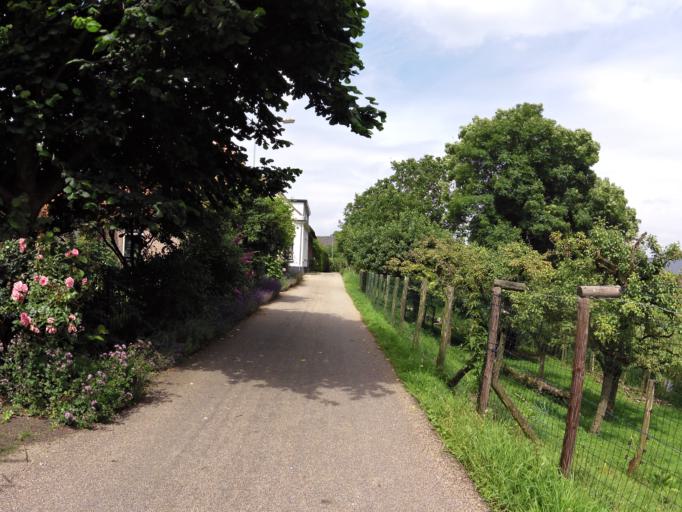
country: NL
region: South Holland
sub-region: Gemeente Leerdam
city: Leerdam
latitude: 51.8757
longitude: 5.1352
